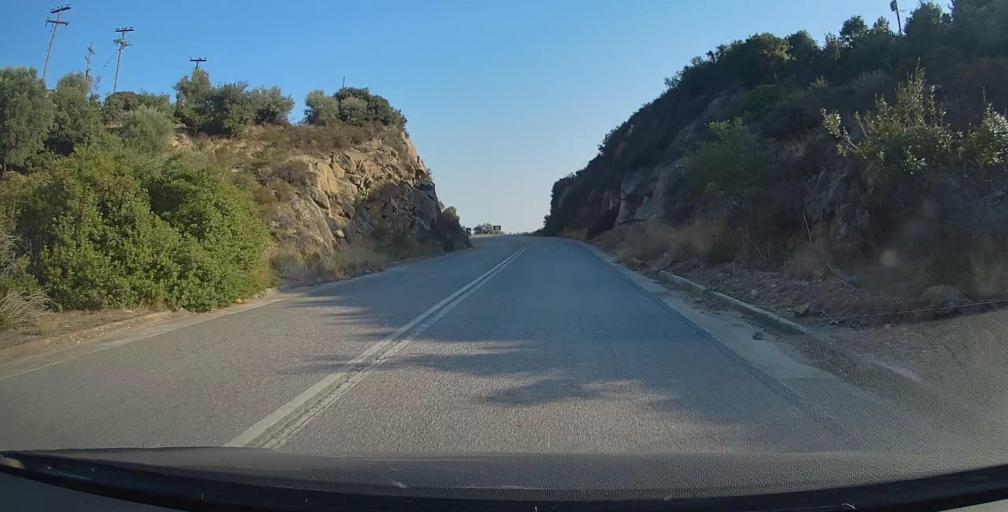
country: GR
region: Central Macedonia
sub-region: Nomos Chalkidikis
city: Sykia
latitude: 40.0003
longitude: 23.8886
